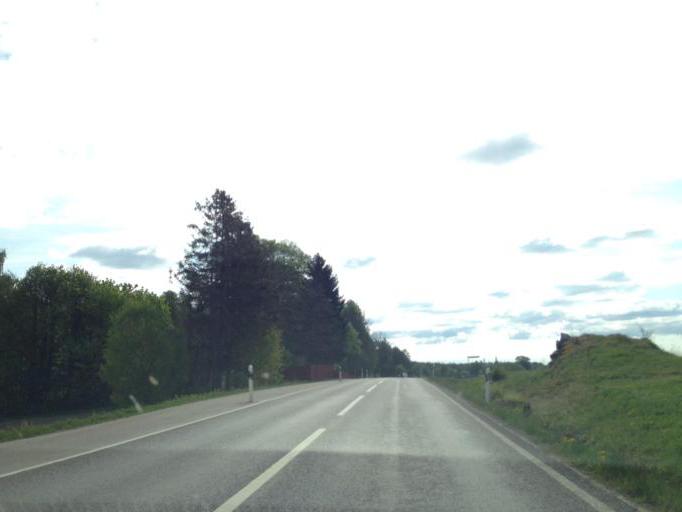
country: SE
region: Soedermanland
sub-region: Nykopings Kommun
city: Stigtomta
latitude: 58.8743
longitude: 16.8824
